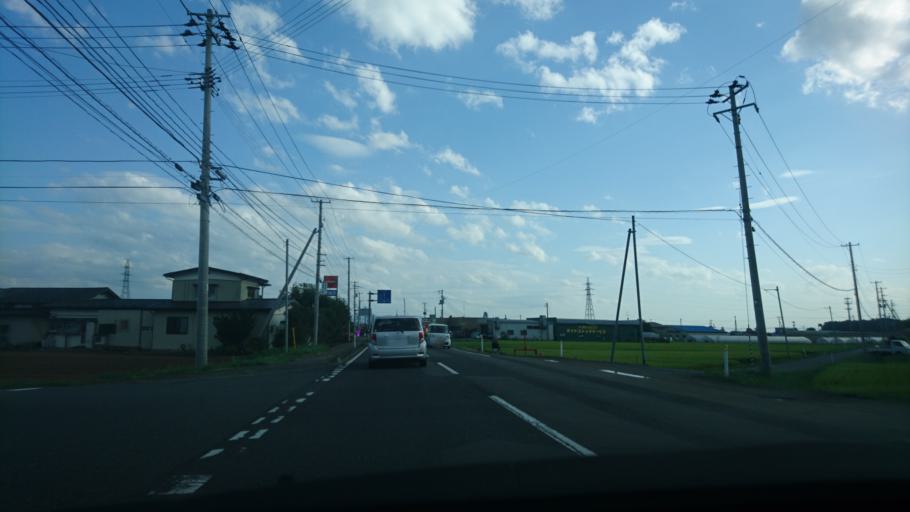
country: JP
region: Iwate
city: Mizusawa
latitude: 39.1607
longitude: 141.1803
